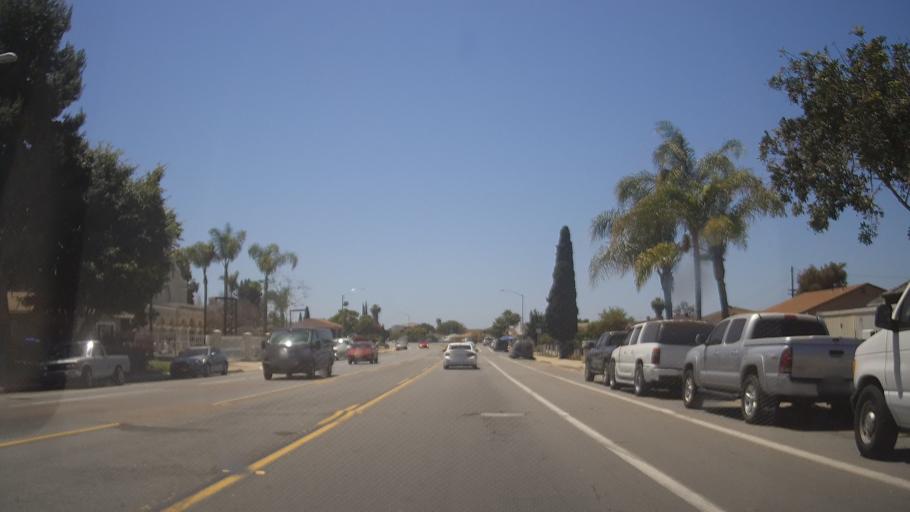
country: US
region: California
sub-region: San Diego County
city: National City
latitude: 32.7069
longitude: -117.0796
